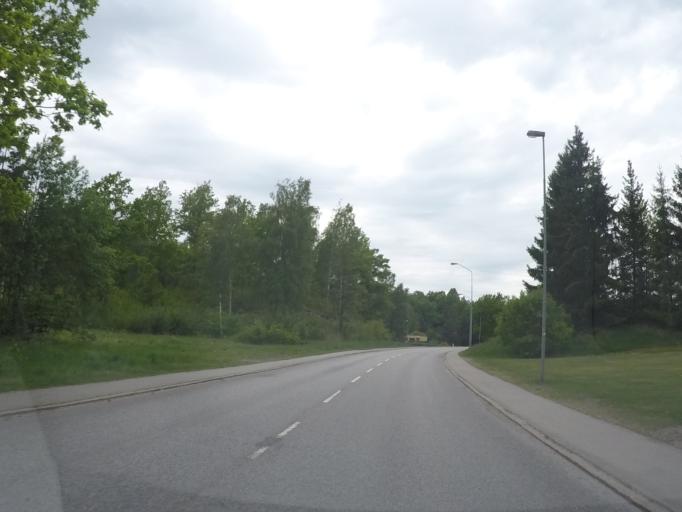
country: SE
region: Soedermanland
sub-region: Flens Kommun
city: Malmkoping
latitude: 59.0716
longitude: 16.8245
